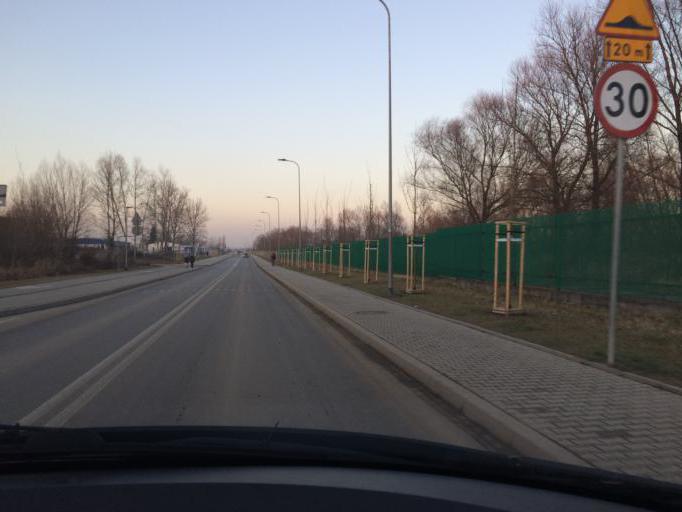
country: PL
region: Lesser Poland Voivodeship
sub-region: Powiat wielicki
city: Czarnochowice
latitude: 50.0253
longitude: 20.0514
